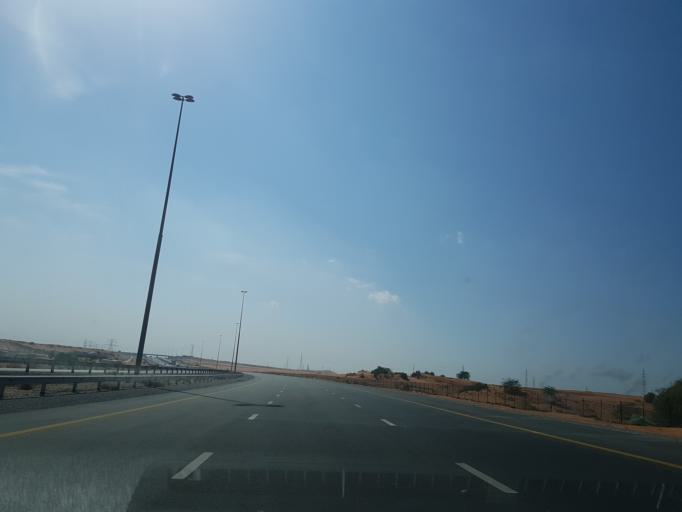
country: AE
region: Ra's al Khaymah
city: Ras al-Khaimah
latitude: 25.7048
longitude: 55.9392
